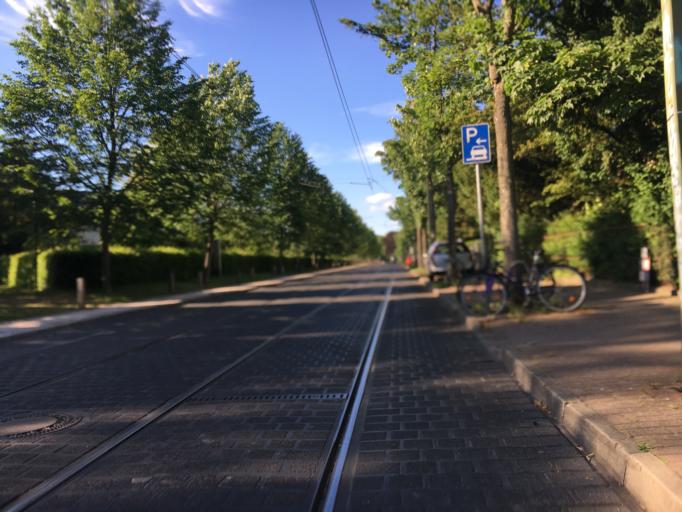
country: DE
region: Brandenburg
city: Potsdam
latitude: 52.4094
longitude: 13.0584
